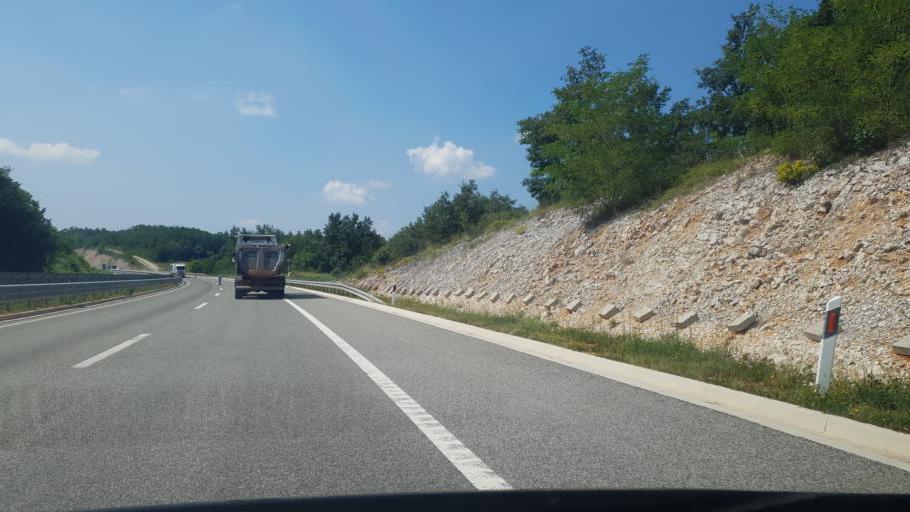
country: HR
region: Istarska
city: Pazin
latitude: 45.2097
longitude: 13.8930
